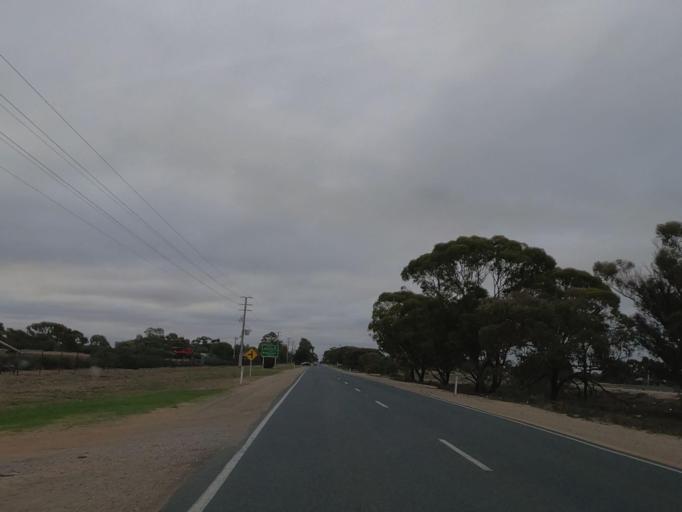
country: AU
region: Victoria
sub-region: Swan Hill
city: Swan Hill
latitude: -35.3879
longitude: 143.5684
